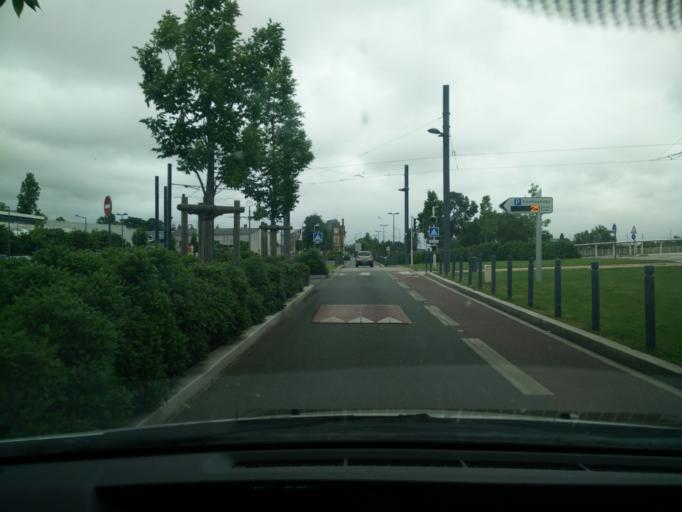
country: FR
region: Pays de la Loire
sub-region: Departement de Maine-et-Loire
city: Angers
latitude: 47.4806
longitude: -0.5544
